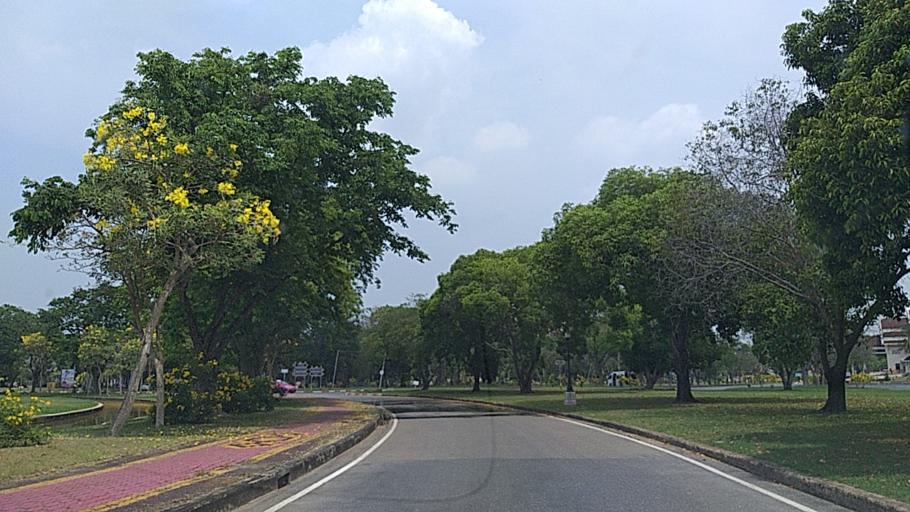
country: TH
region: Bangkok
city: Thawi Watthana
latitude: 13.7810
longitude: 100.3252
